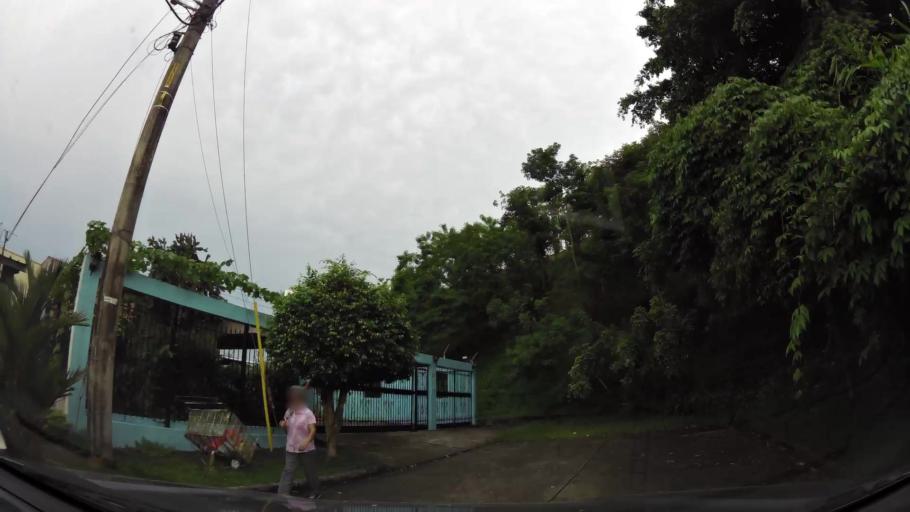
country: PA
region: Panama
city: Panama
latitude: 9.0143
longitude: -79.5364
